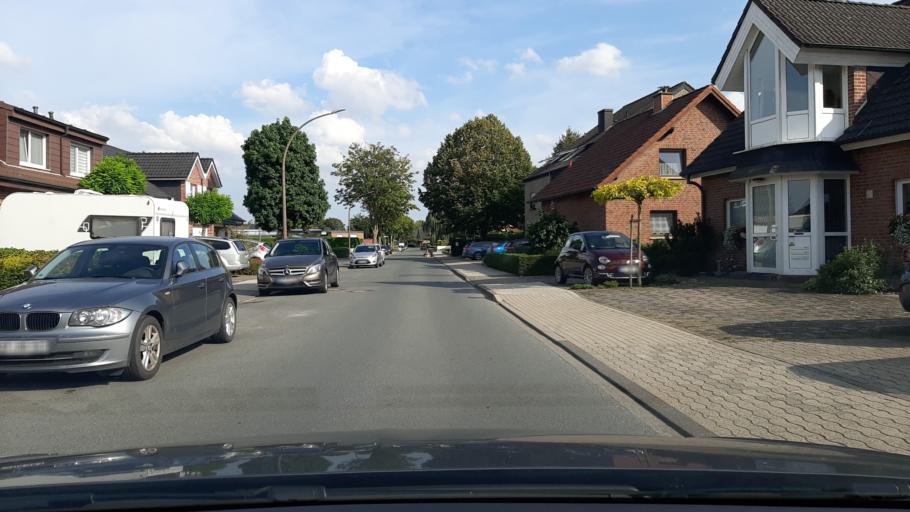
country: DE
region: North Rhine-Westphalia
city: Ahlen
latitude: 51.7767
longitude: 7.9002
